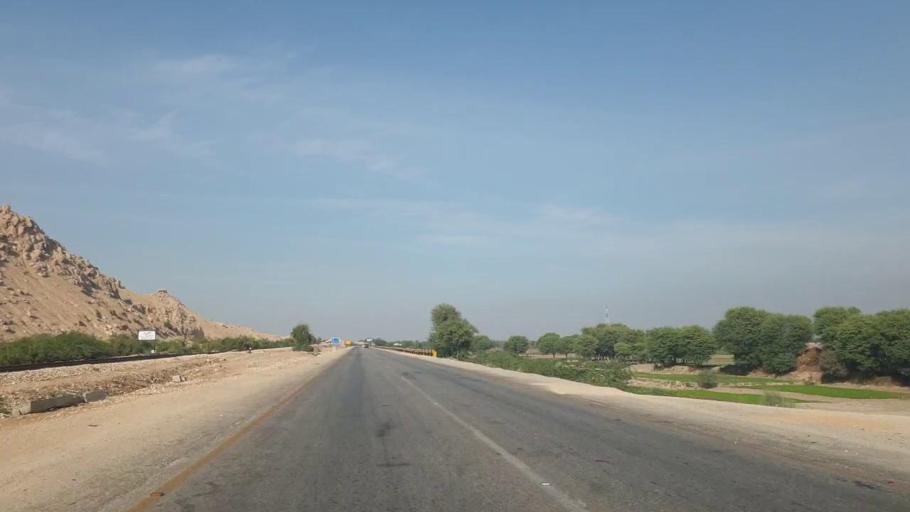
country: PK
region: Sindh
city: Sehwan
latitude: 26.2919
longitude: 67.8943
